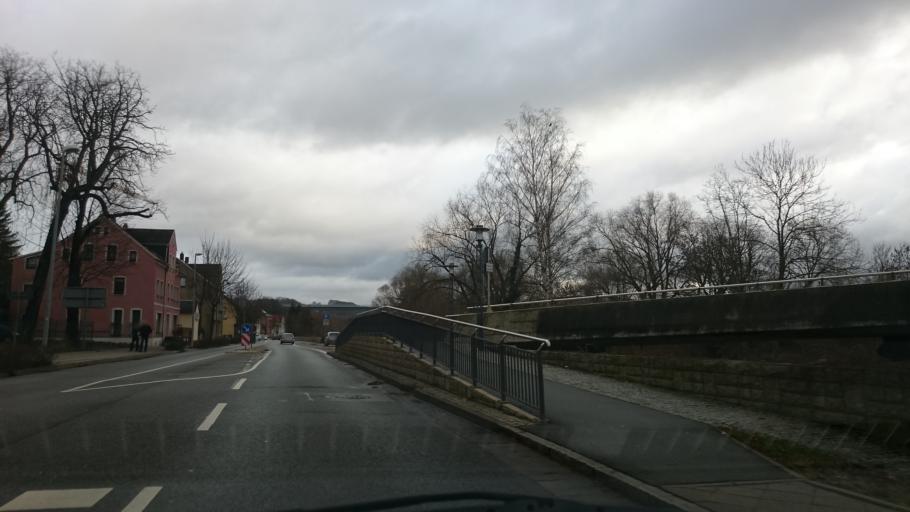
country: DE
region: Saxony
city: Wilkau-Hasslau
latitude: 50.6763
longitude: 12.5152
